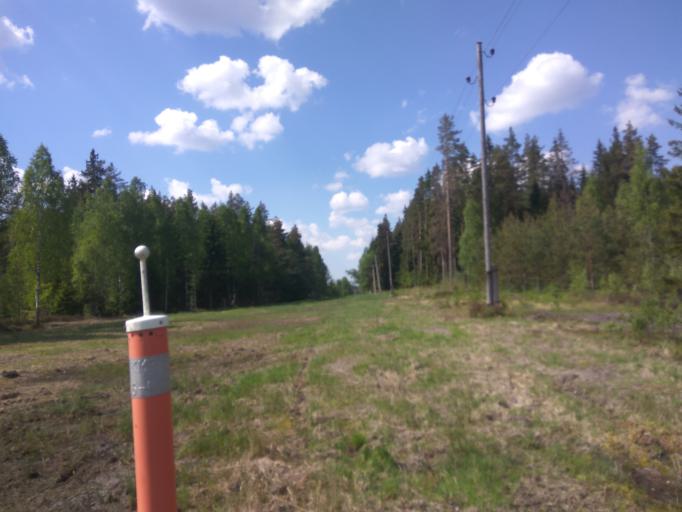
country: LV
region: Kuldigas Rajons
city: Kuldiga
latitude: 57.1858
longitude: 21.9921
